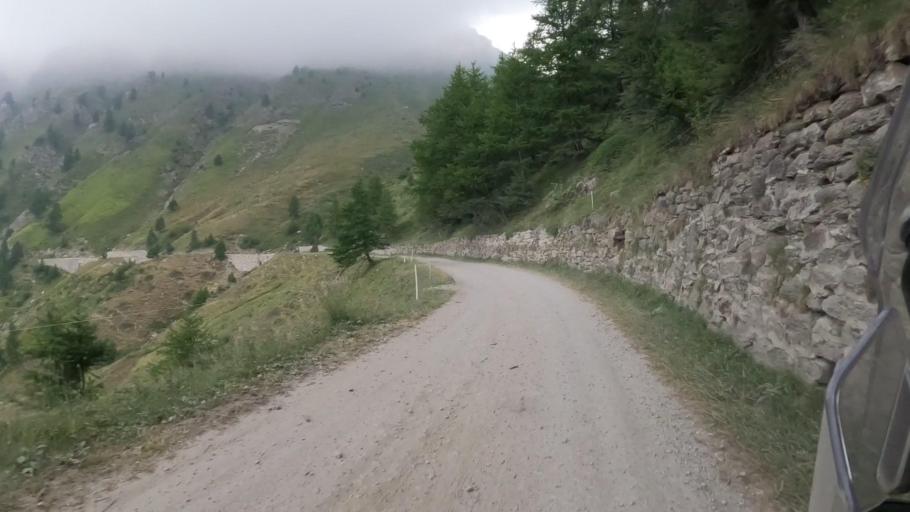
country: IT
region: Piedmont
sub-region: Provincia di Torino
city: Usseaux
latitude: 45.0612
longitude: 6.9992
